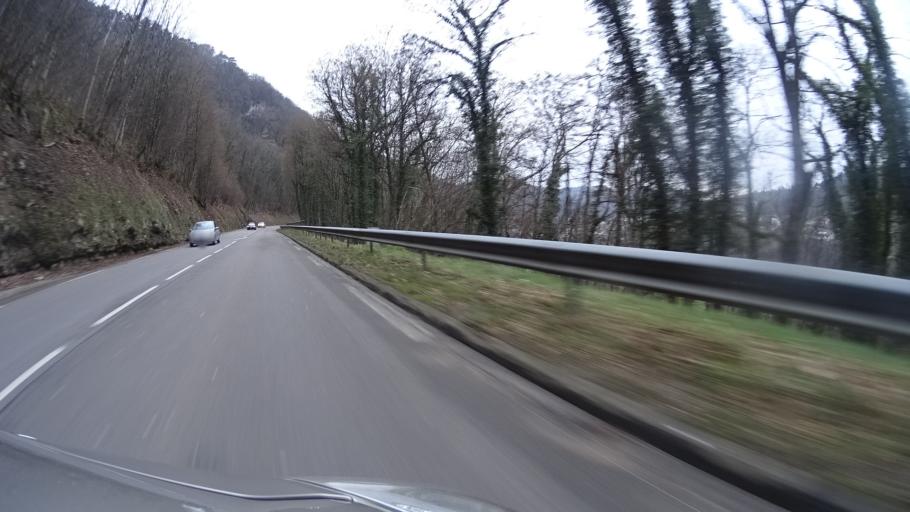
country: FR
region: Franche-Comte
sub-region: Departement du Doubs
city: Morre
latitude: 47.2287
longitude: 6.0578
